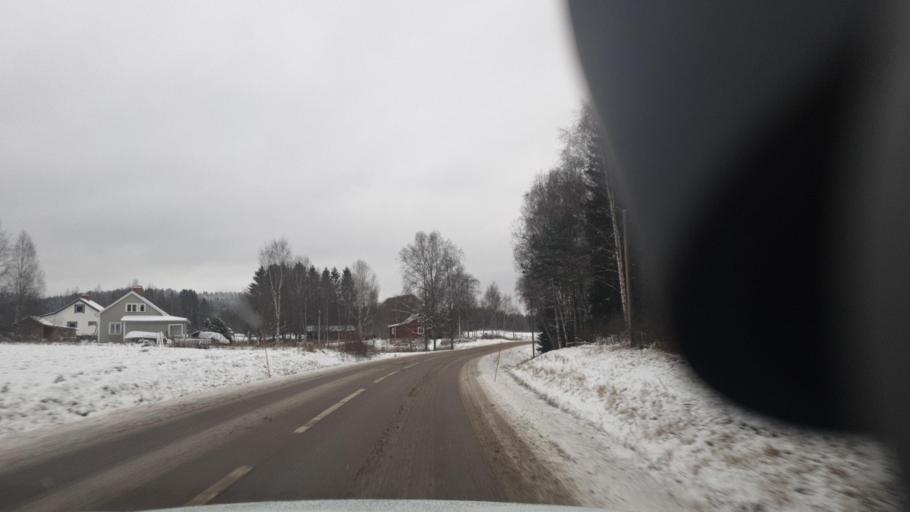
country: SE
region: Vaermland
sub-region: Arjangs Kommun
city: Arjaeng
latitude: 59.6016
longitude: 12.1520
